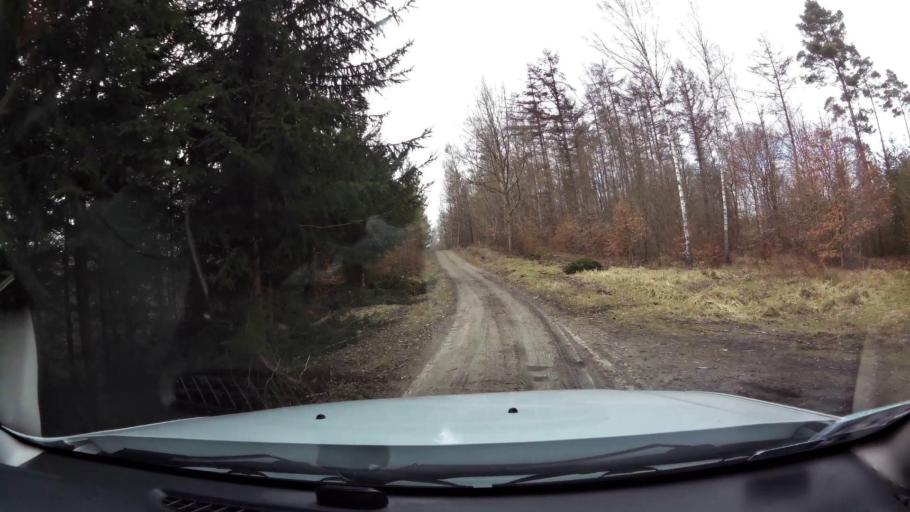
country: PL
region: West Pomeranian Voivodeship
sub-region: Powiat drawski
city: Drawsko Pomorskie
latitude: 53.5042
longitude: 15.7063
